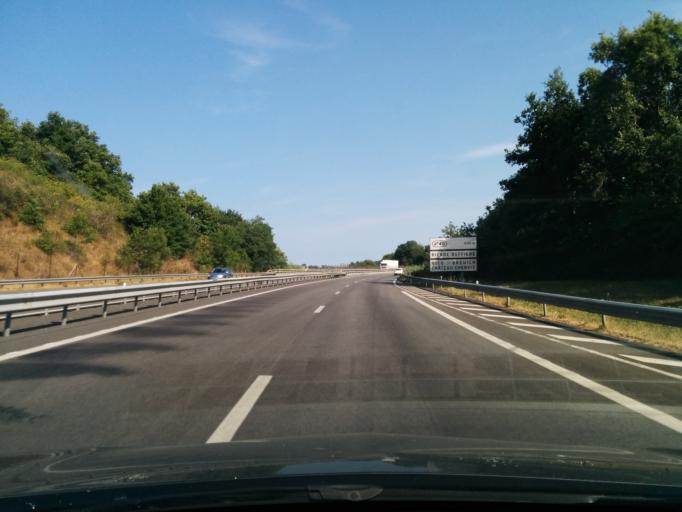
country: FR
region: Limousin
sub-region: Departement de la Haute-Vienne
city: Pierre-Buffiere
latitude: 45.6976
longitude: 1.3624
